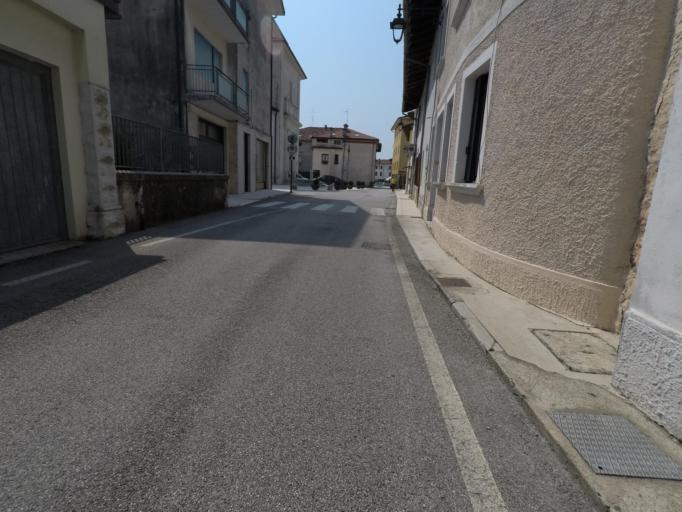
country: IT
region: Friuli Venezia Giulia
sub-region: Provincia di Pordenone
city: Montereale Valcellina
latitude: 46.1614
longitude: 12.6613
